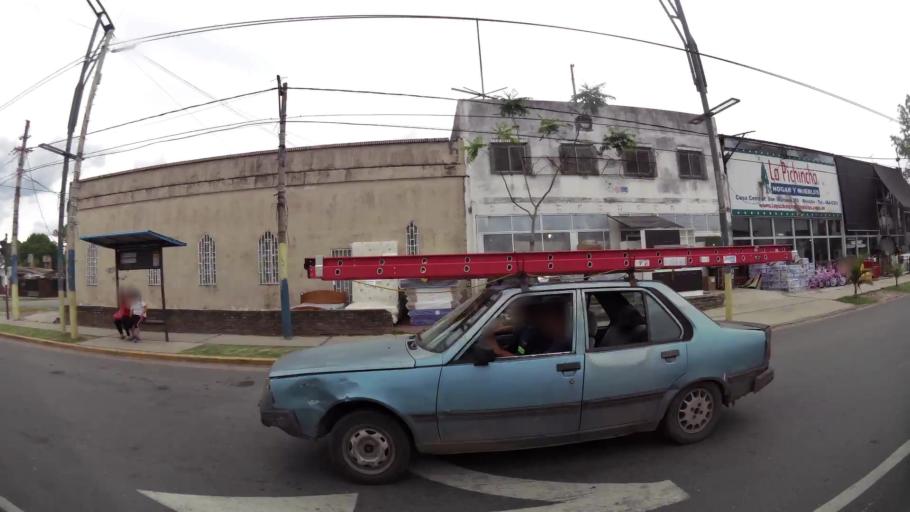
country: AR
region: Santa Fe
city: Gobernador Galvez
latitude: -33.0120
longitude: -60.6515
